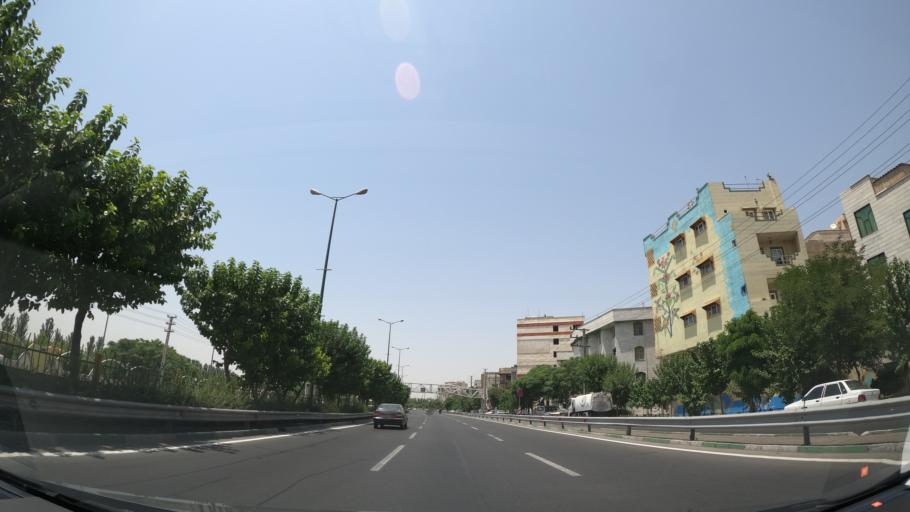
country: IR
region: Tehran
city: Tehran
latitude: 35.6511
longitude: 51.3873
